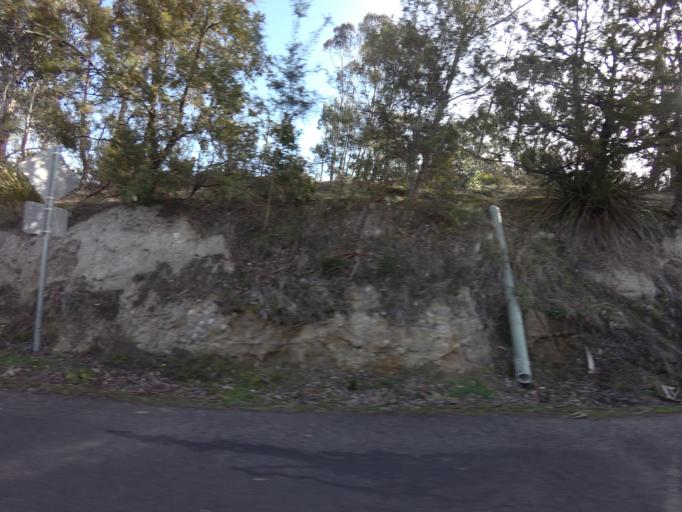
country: AU
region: Tasmania
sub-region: Kingborough
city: Kettering
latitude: -43.1211
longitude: 147.2560
